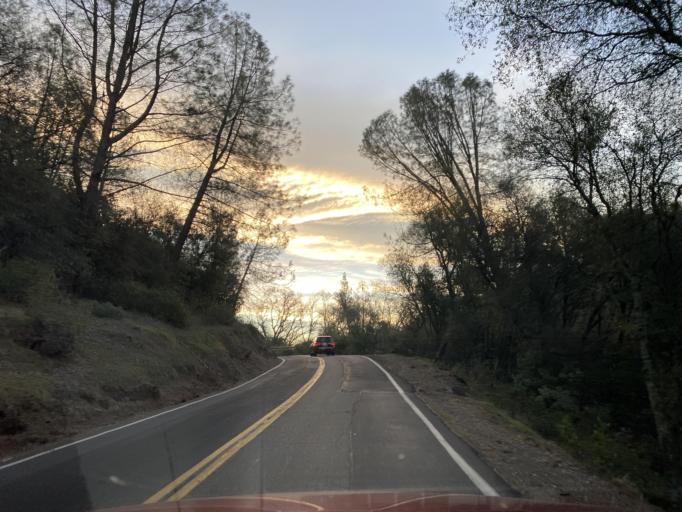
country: US
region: California
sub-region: Amador County
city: Plymouth
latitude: 38.5016
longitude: -120.7467
